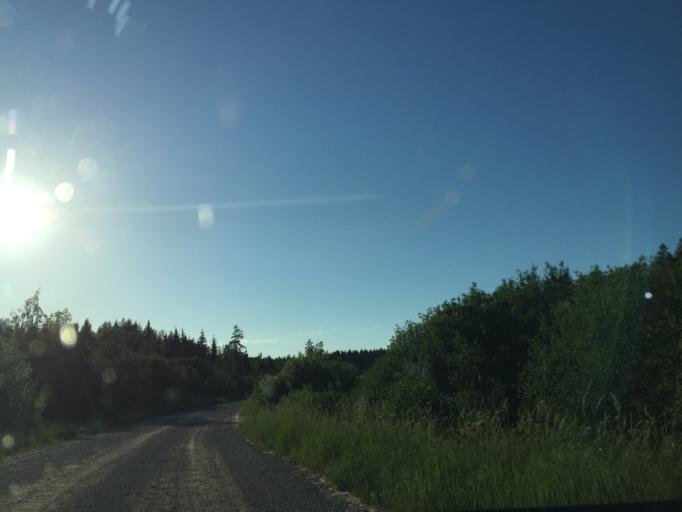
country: LV
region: Talsu Rajons
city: Sabile
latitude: 56.8599
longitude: 22.6684
